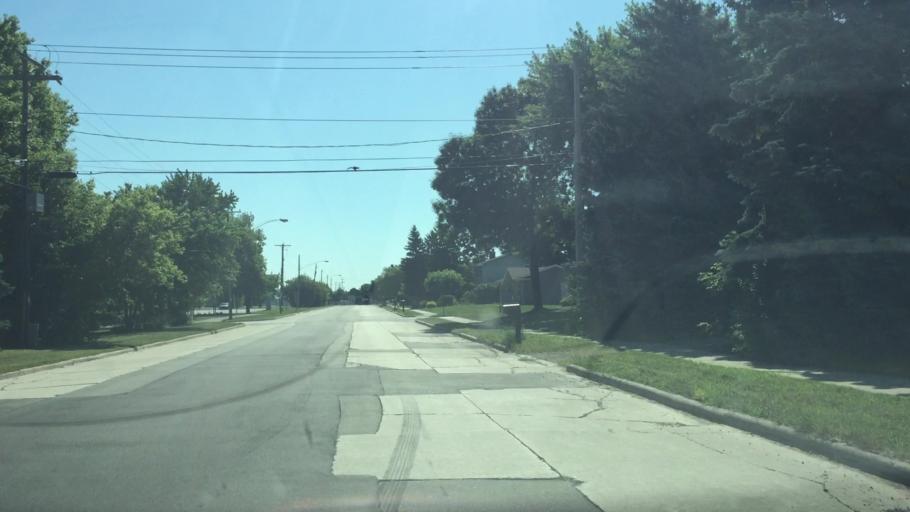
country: US
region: Wisconsin
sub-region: Winnebago County
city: Menasha
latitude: 44.2226
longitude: -88.4345
